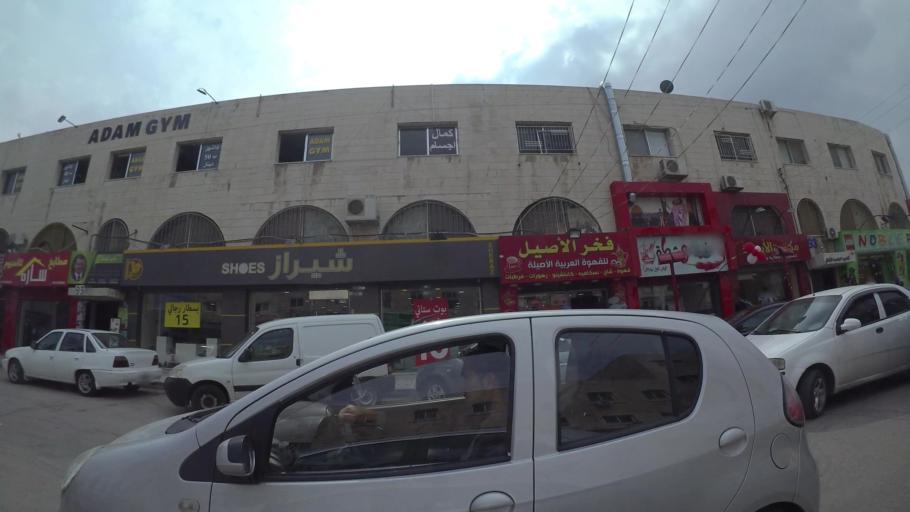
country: JO
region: Amman
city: Umm as Summaq
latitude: 31.8928
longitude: 35.8425
